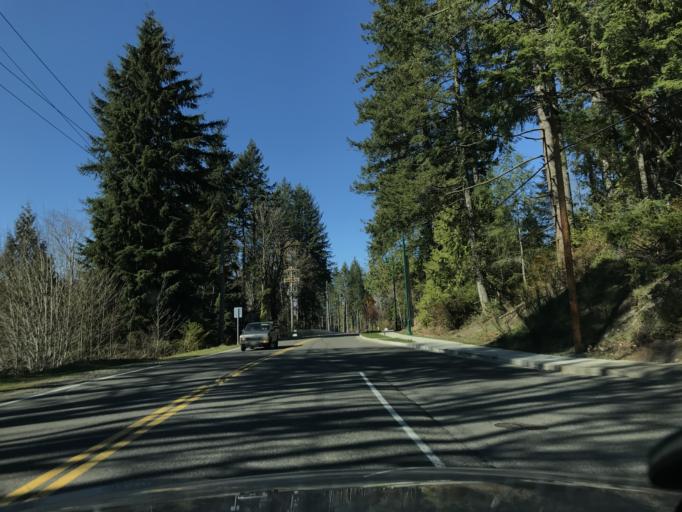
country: US
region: Washington
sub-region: Pierce County
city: Gig Harbor
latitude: 47.3463
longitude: -122.6024
